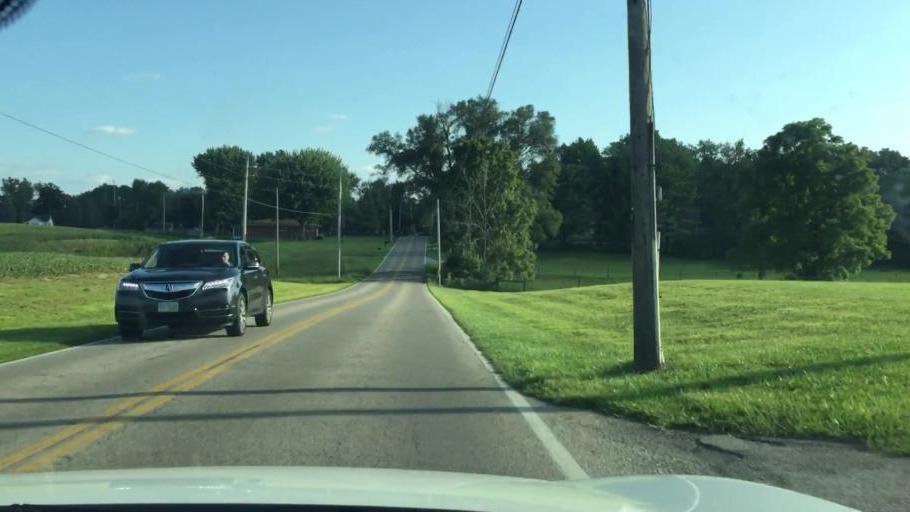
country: US
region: Ohio
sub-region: Clark County
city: Northridge
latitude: 39.9419
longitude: -83.7299
